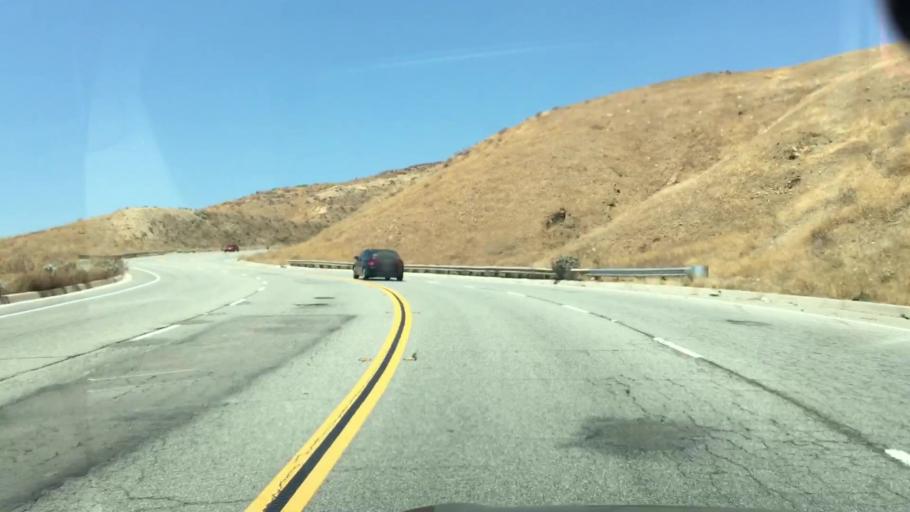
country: US
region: California
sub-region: San Bernardino County
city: Muscoy
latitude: 34.1574
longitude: -117.3217
